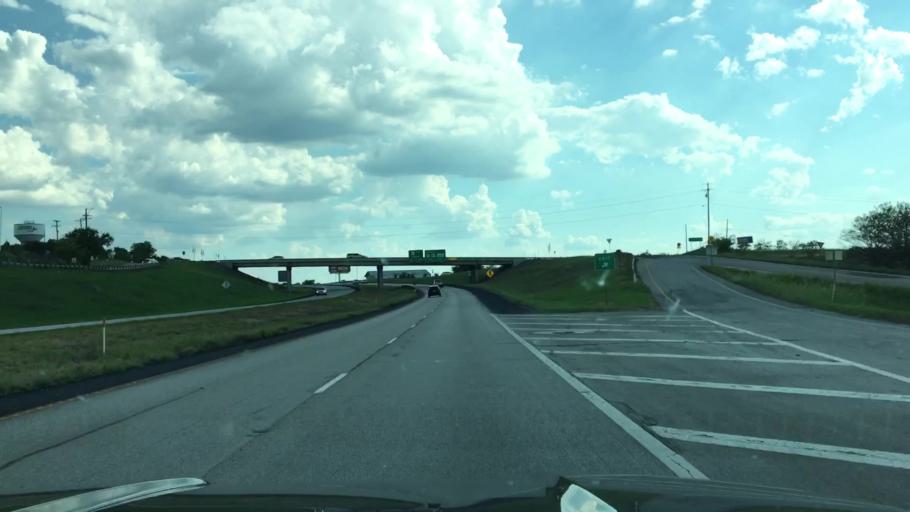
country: US
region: Texas
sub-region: Wise County
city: Rhome
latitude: 33.0578
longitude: -97.4782
